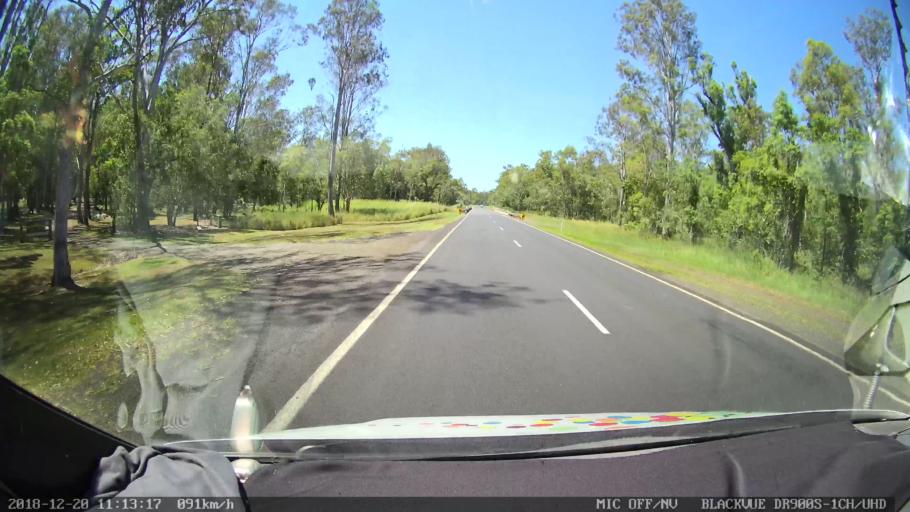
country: AU
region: New South Wales
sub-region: Richmond Valley
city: Casino
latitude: -28.9856
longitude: 153.0100
